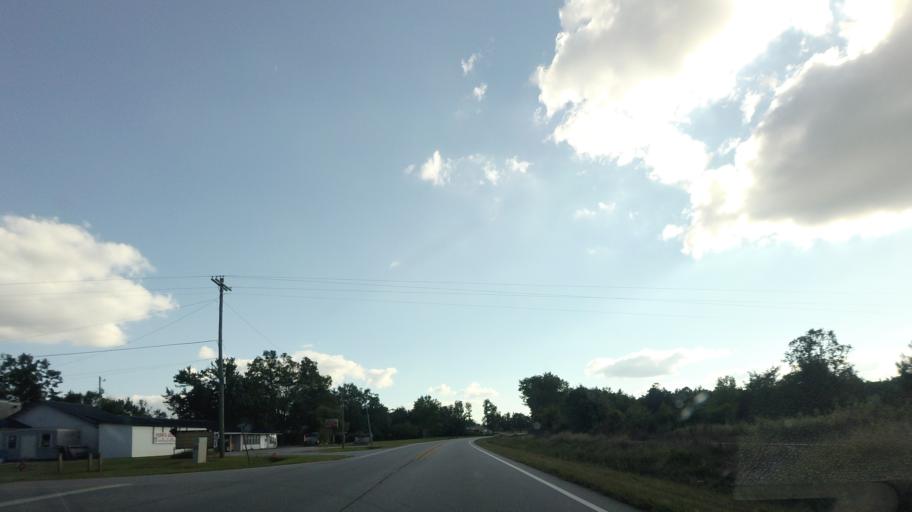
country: US
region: Georgia
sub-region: Lamar County
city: Barnesville
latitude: 33.0051
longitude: -84.1917
